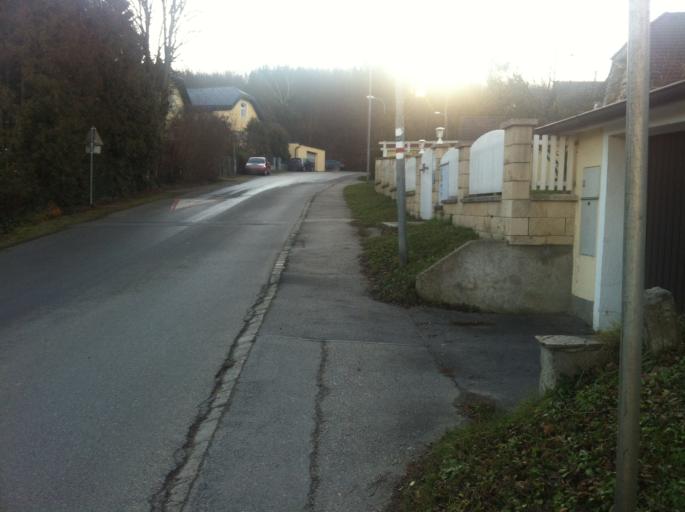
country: AT
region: Lower Austria
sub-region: Politischer Bezirk Wien-Umgebung
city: Gablitz
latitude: 48.2241
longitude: 16.1590
